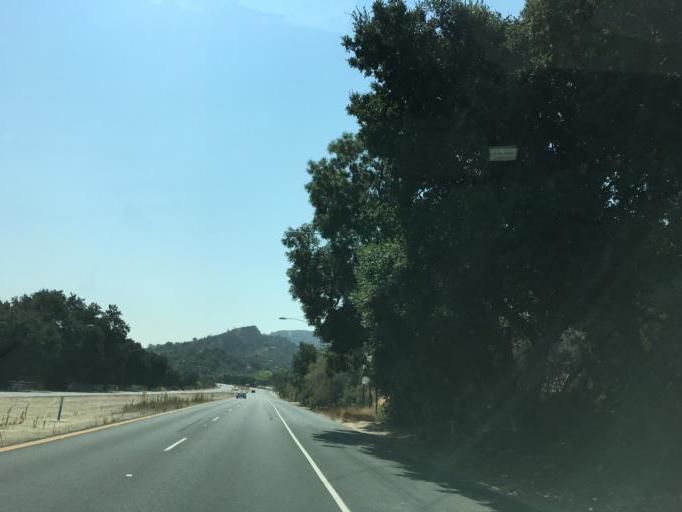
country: US
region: California
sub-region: Los Angeles County
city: Santa Clarita
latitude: 34.3538
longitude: -118.5512
